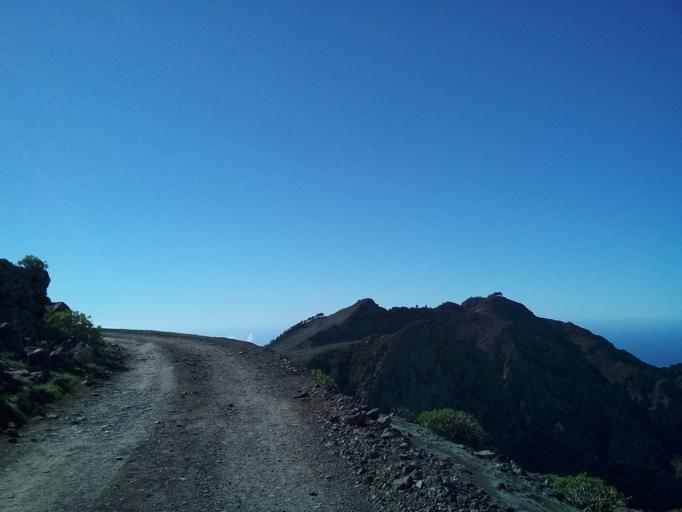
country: ES
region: Canary Islands
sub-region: Provincia de Santa Cruz de Tenerife
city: Vallehermosa
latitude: 28.1280
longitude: -17.3278
